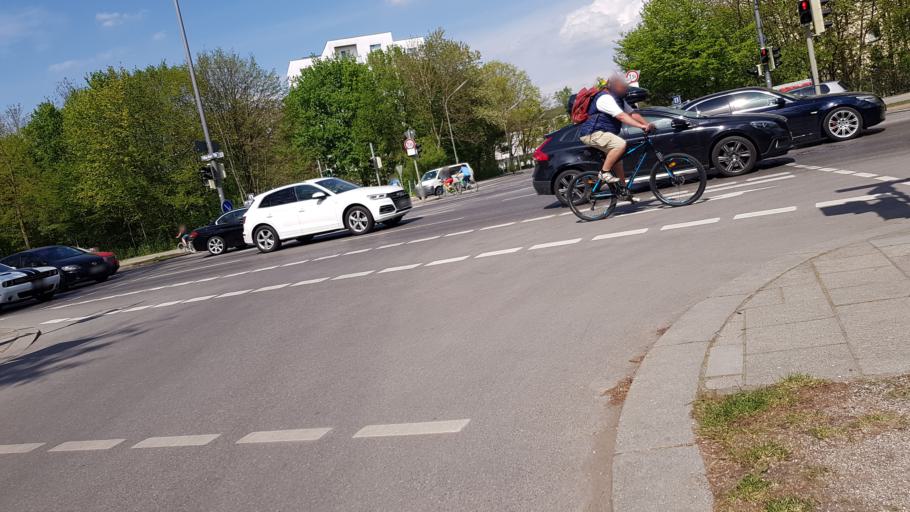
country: DE
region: Bavaria
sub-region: Upper Bavaria
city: Karlsfeld
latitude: 48.1777
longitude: 11.4946
